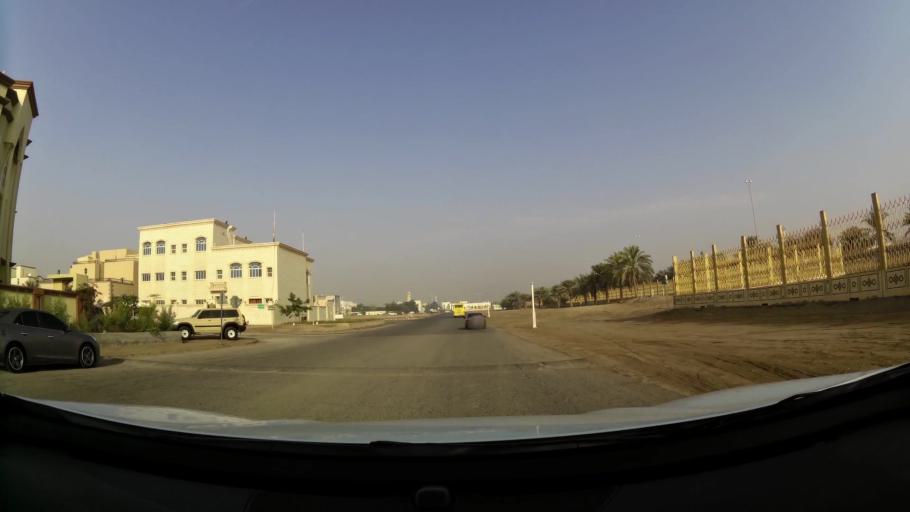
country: AE
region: Abu Dhabi
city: Abu Dhabi
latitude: 24.2911
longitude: 54.6337
